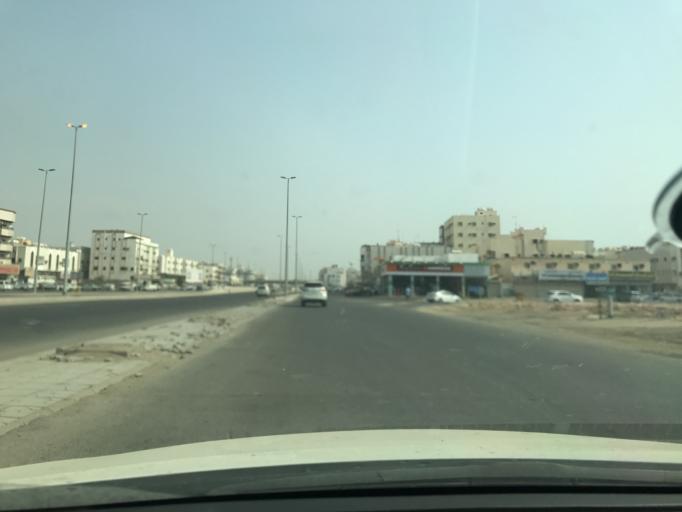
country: SA
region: Makkah
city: Jeddah
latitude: 21.6243
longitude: 39.1841
